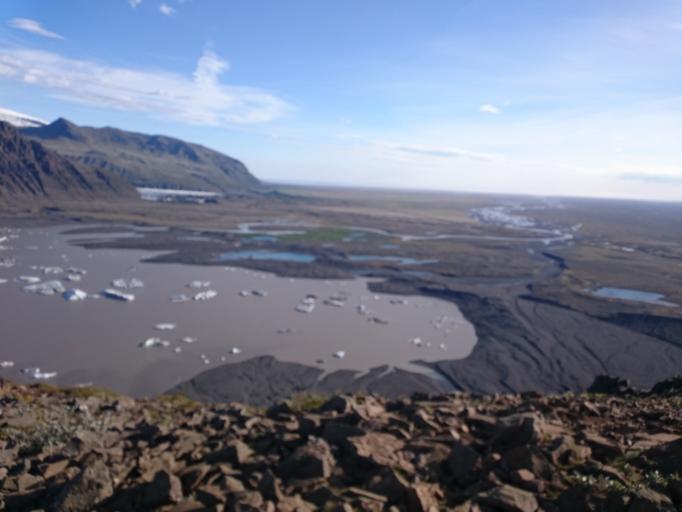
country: IS
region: East
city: Hoefn
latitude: 64.0307
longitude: -16.9373
